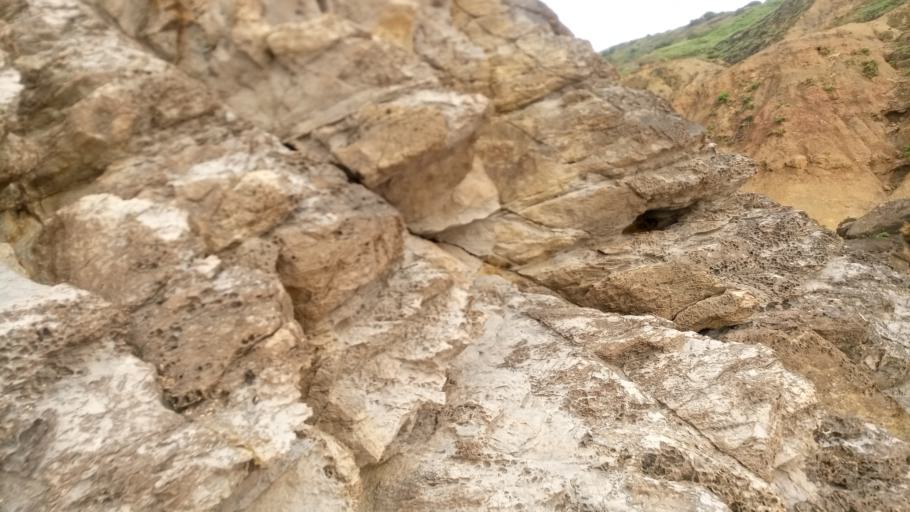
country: PT
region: Leiria
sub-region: Caldas da Rainha
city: Caldas da Rainha
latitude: 39.4893
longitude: -9.1810
